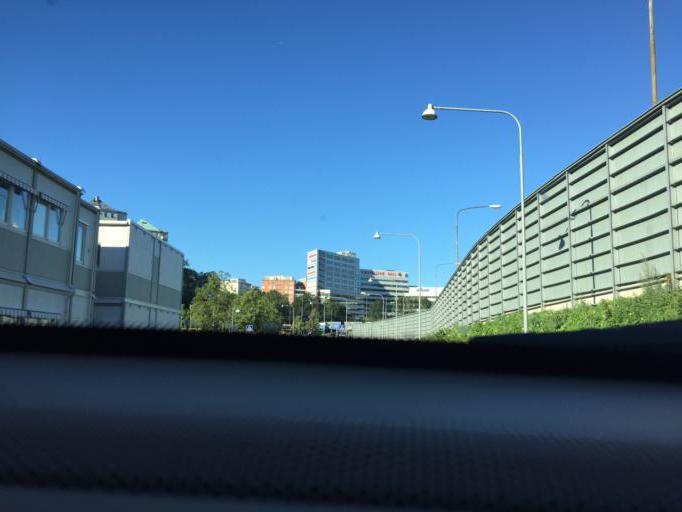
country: SE
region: Stockholm
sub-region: Stockholms Kommun
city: OEstermalm
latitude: 59.3102
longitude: 18.1052
